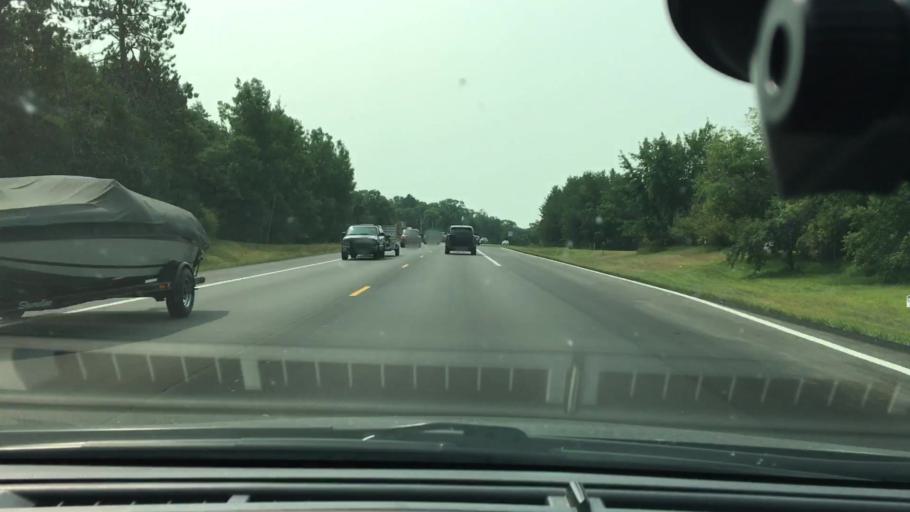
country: US
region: Minnesota
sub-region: Crow Wing County
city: Brainerd
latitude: 46.4391
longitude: -94.1715
